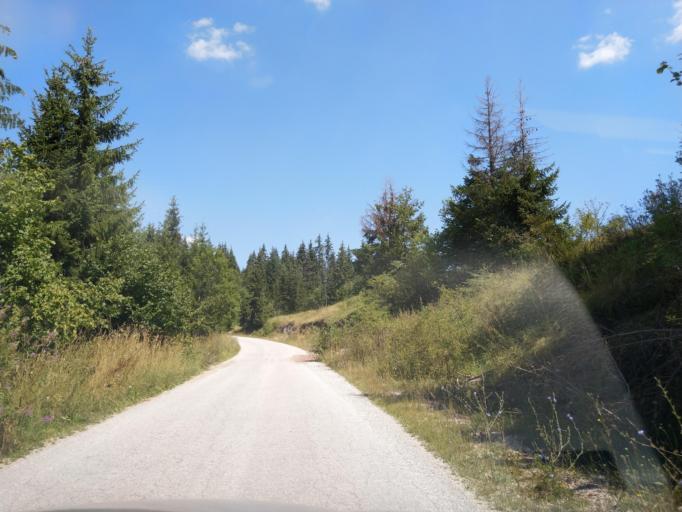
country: RS
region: Central Serbia
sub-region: Zlatiborski Okrug
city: Nova Varos
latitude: 43.4746
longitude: 19.9654
